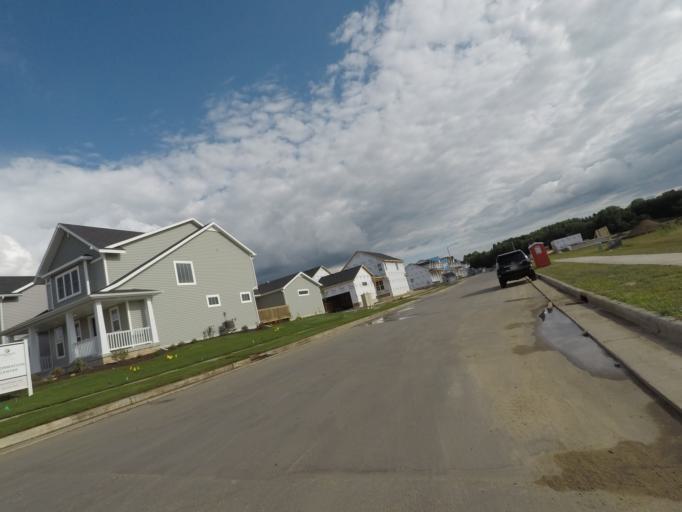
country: US
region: Wisconsin
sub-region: Dane County
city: Verona
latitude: 43.0509
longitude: -89.5499
